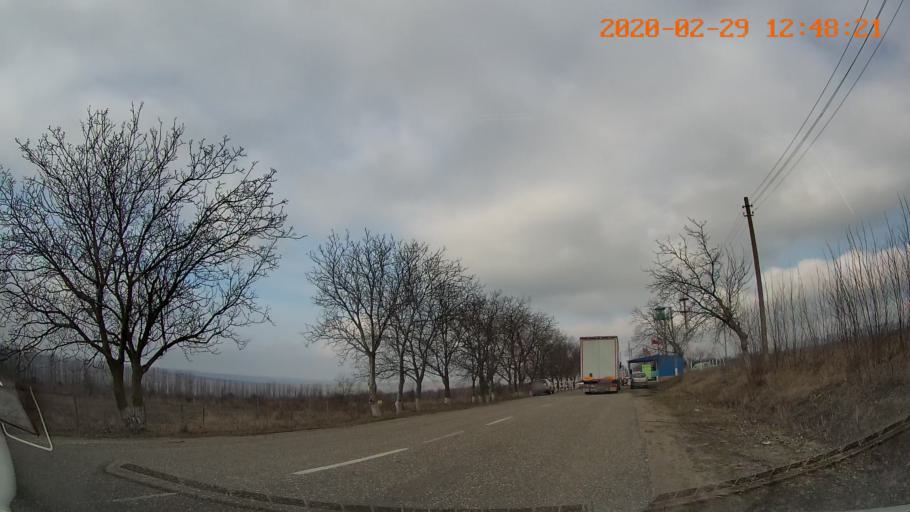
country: MD
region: Telenesti
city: Camenca
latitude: 48.1271
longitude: 28.7411
